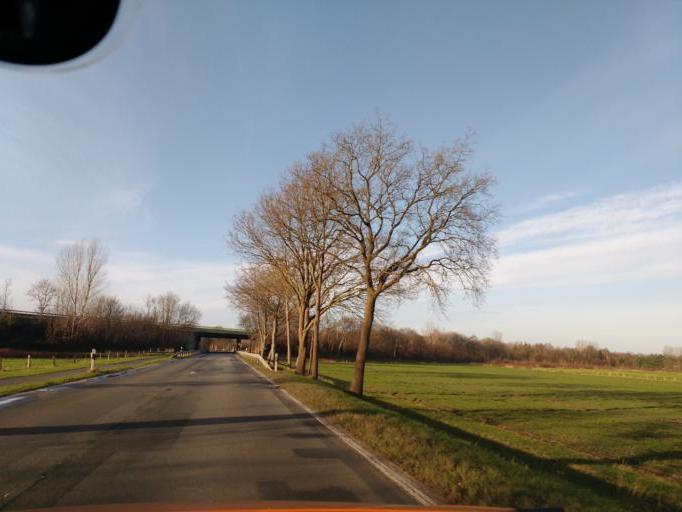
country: DE
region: Lower Saxony
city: Oldenburg
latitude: 53.1018
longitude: 8.2875
